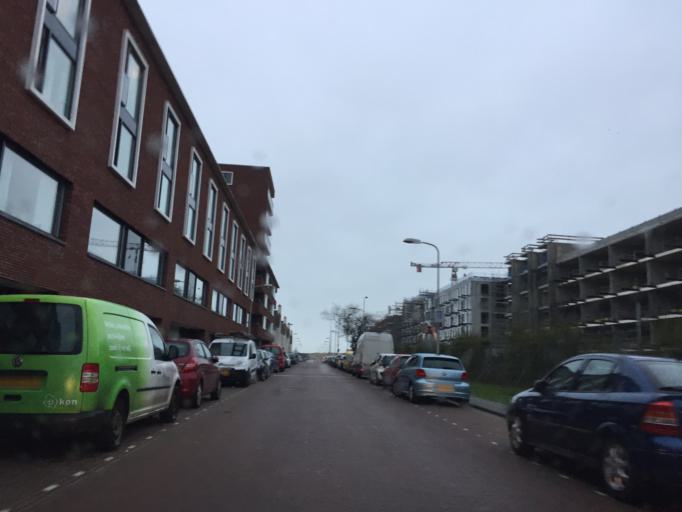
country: NL
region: South Holland
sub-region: Gemeente Den Haag
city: Scheveningen
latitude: 52.0935
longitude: 4.2620
